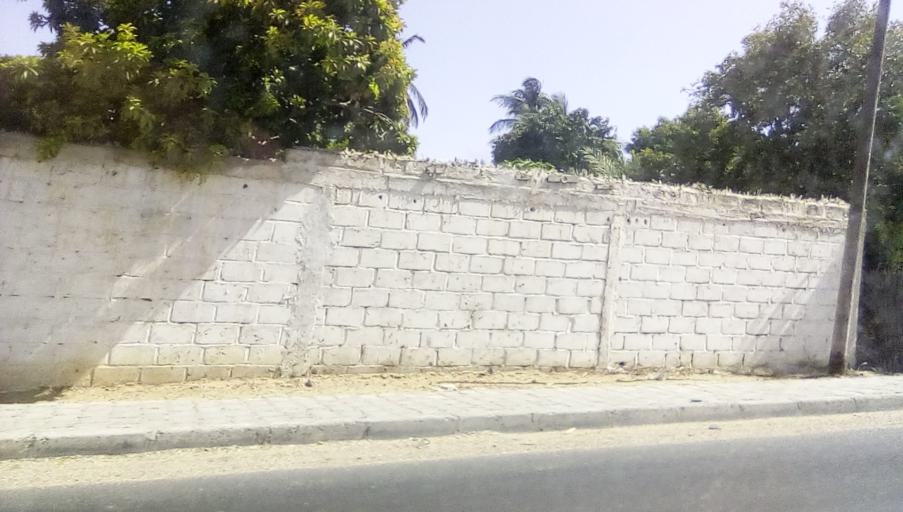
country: SN
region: Saint-Louis
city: Saint-Louis
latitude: 16.0381
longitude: -16.4608
